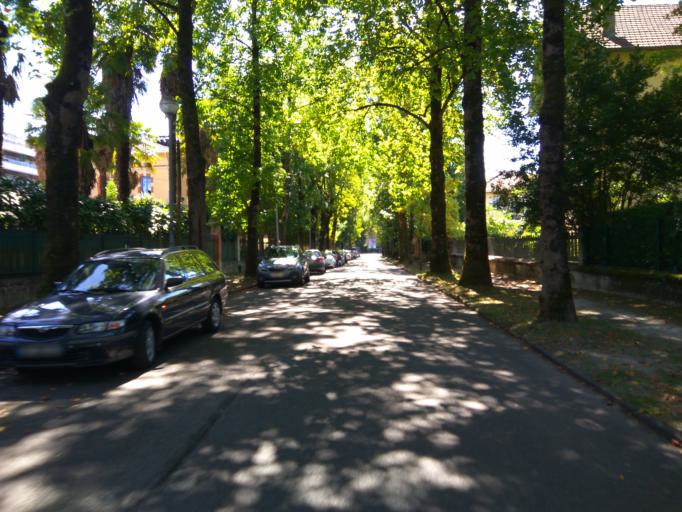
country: FR
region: Aquitaine
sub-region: Departement des Pyrenees-Atlantiques
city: Pau
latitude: 43.3036
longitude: -0.3548
